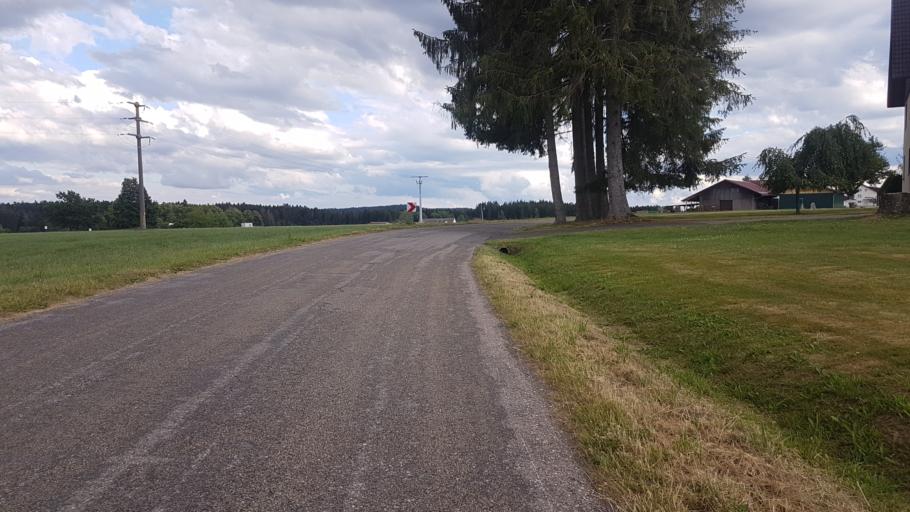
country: DE
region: Baden-Wuerttemberg
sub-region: Freiburg Region
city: Unterkirnach
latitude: 48.0277
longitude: 8.4082
